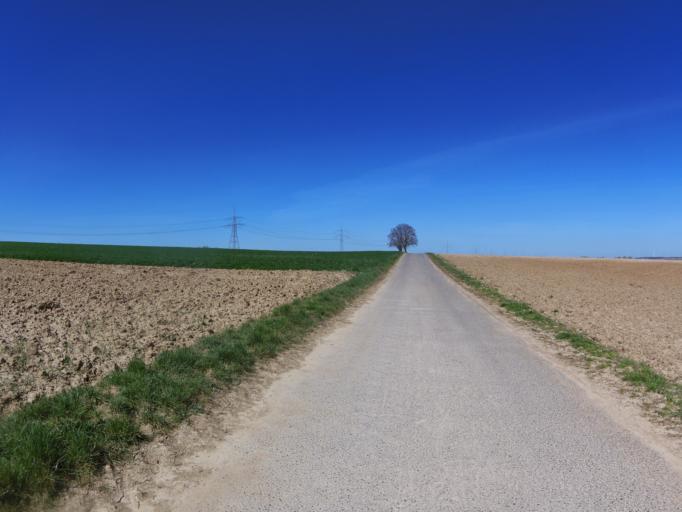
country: DE
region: Bavaria
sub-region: Regierungsbezirk Unterfranken
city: Biebelried
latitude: 49.8098
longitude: 10.0875
